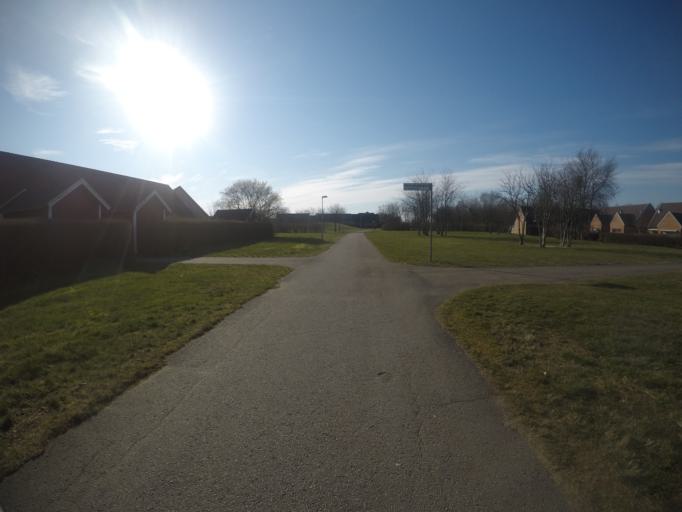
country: SE
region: Halland
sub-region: Laholms Kommun
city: Laholm
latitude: 56.5026
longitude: 13.0606
